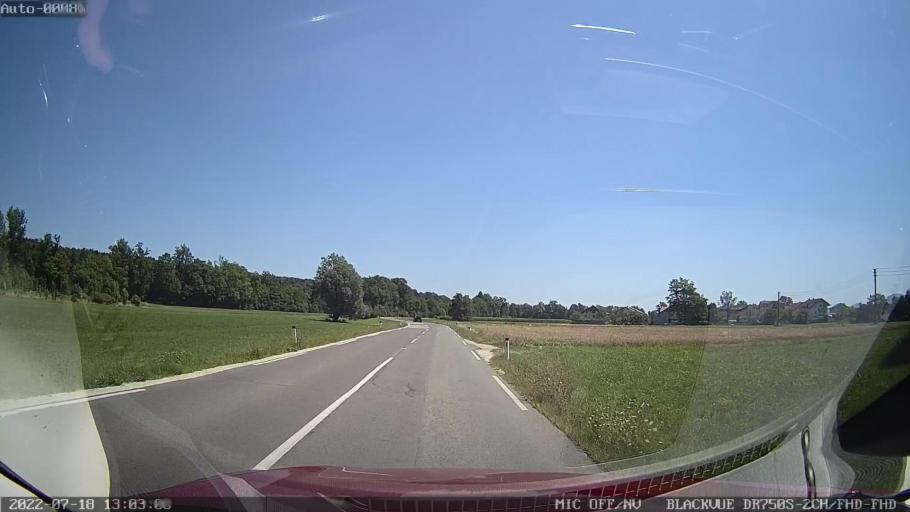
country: SI
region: Brezovica
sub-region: Opstina Ljubljana-Vic-Rudnik
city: Brezovica pri Ljubljani
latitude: 46.0507
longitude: 14.4278
